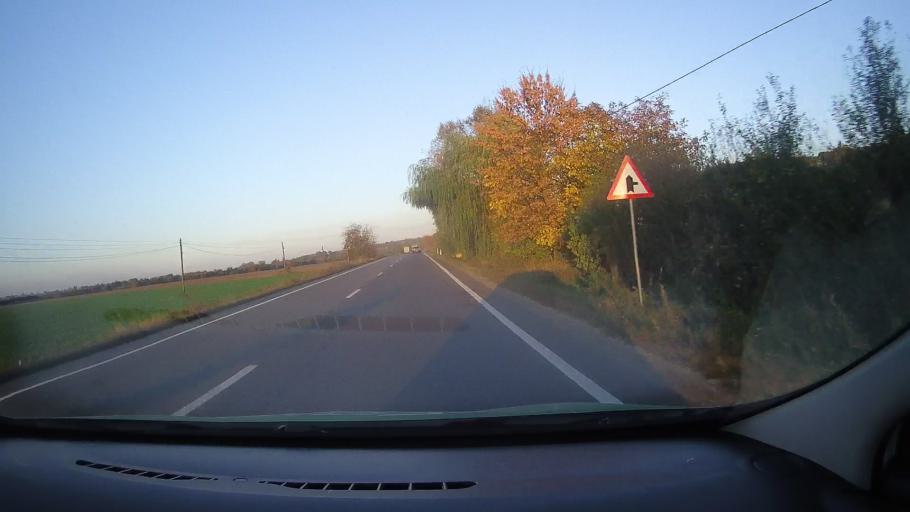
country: RO
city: Dioszeg
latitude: 47.2880
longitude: 21.9986
